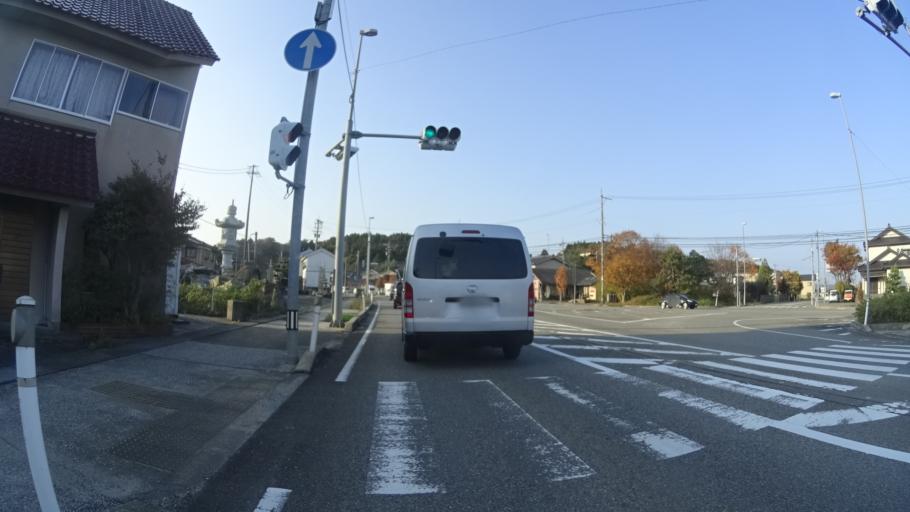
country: JP
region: Ishikawa
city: Nanao
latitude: 37.0562
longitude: 136.9533
